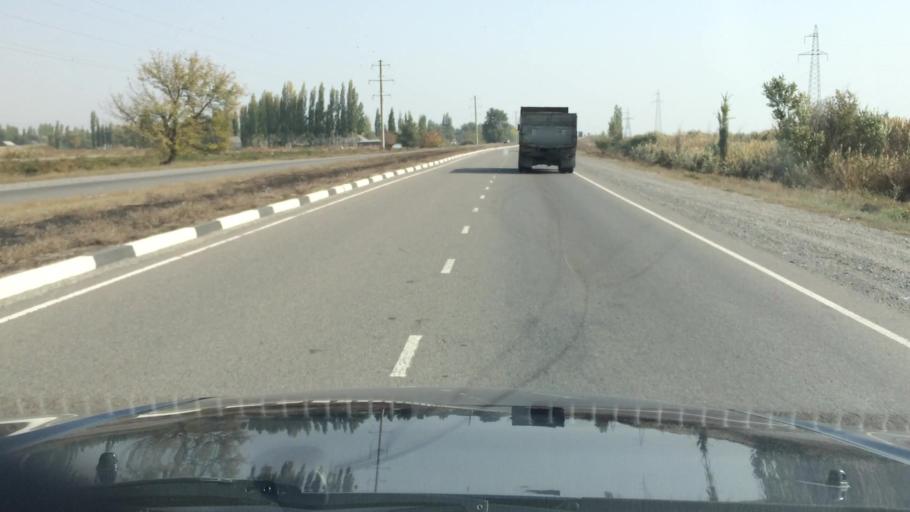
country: KG
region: Chuy
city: Kant
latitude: 42.9680
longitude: 74.8274
